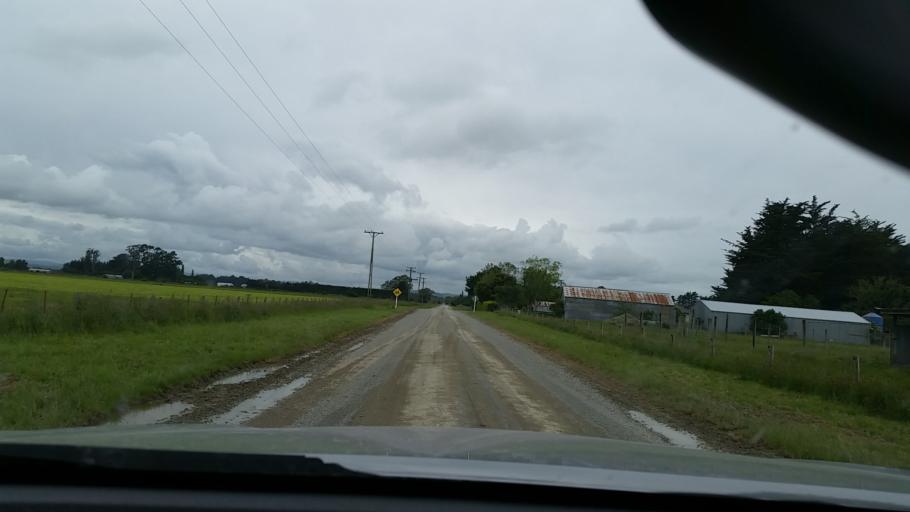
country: NZ
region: Southland
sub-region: Southland District
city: Winton
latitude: -46.1837
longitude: 168.2821
